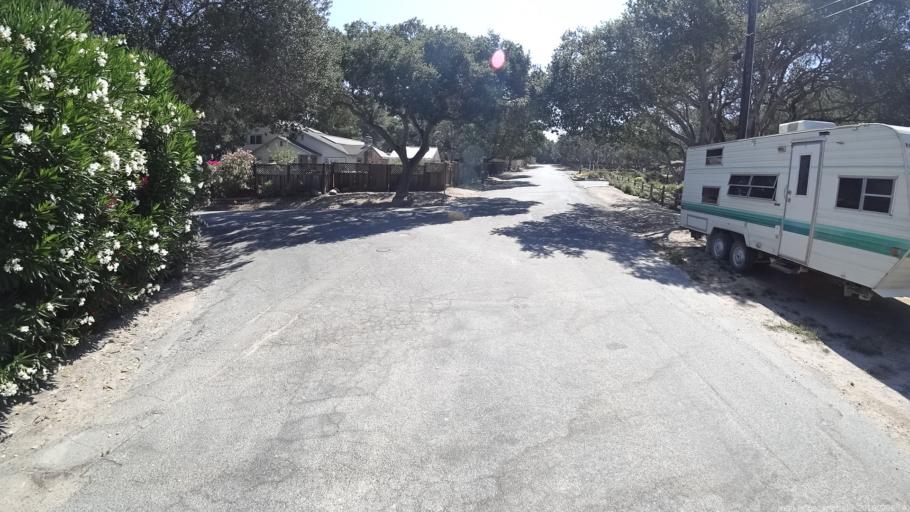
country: US
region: California
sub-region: Monterey County
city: Salinas
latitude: 36.5817
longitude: -121.6328
